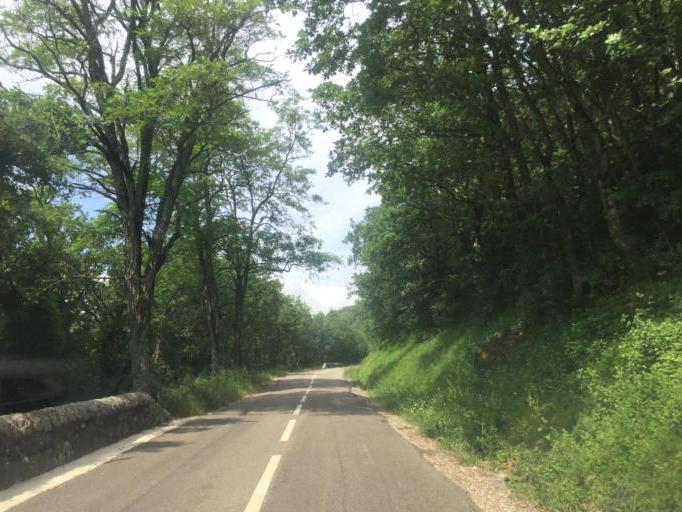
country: FR
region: Rhone-Alpes
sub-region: Departement de l'Ardeche
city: Villeneuve-de-Berg
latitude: 44.6269
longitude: 4.5450
